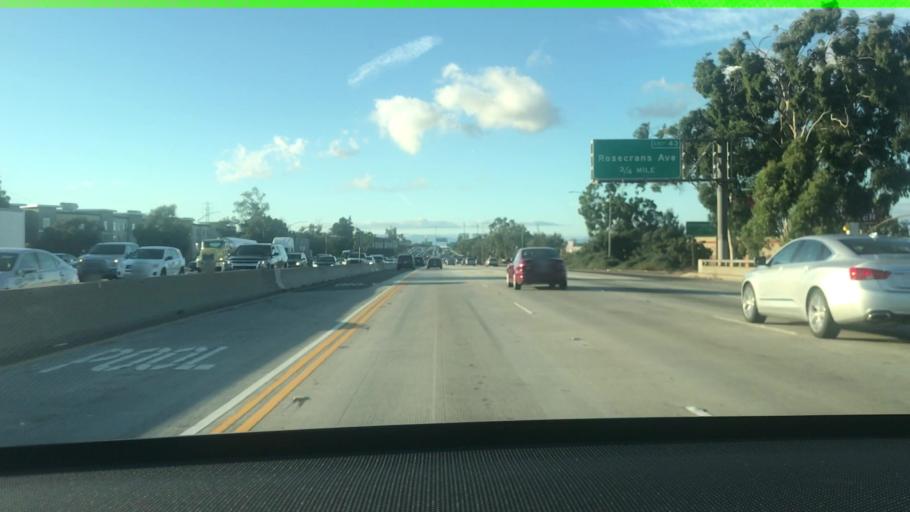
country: US
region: California
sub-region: Los Angeles County
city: Lawndale
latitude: 33.8908
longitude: -118.3612
